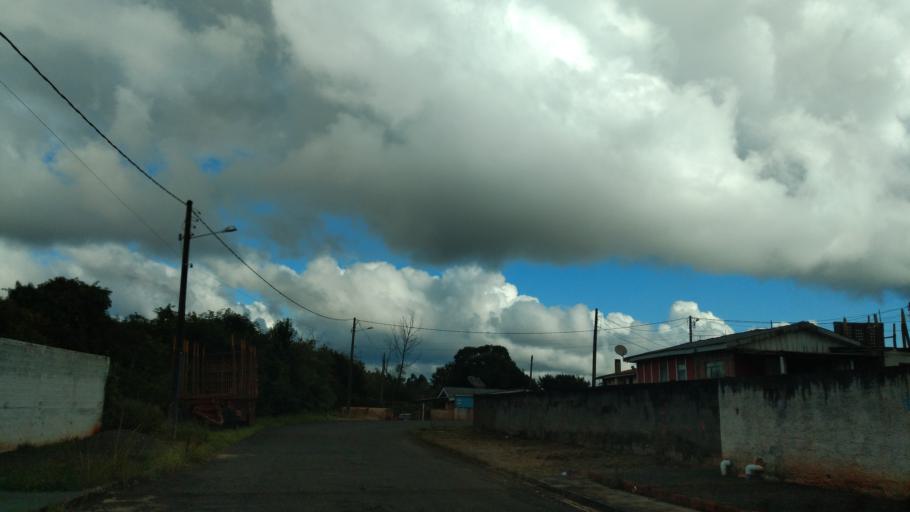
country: BR
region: Parana
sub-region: Guarapuava
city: Guarapuava
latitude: -25.3972
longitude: -51.4885
